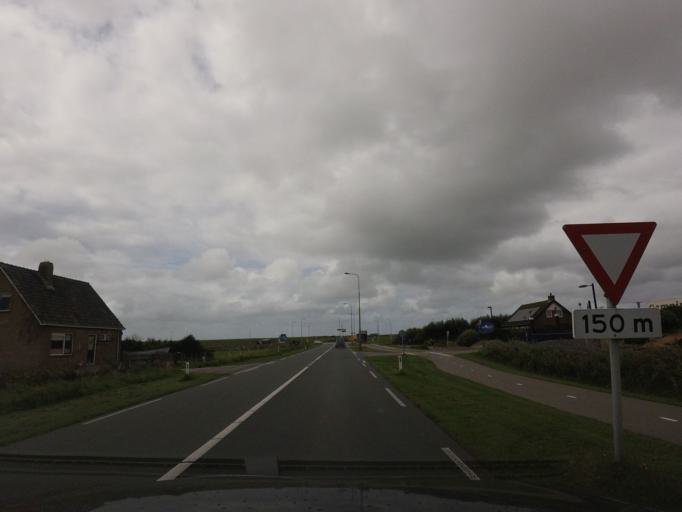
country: NL
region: North Holland
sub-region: Gemeente Schagen
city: Harenkarspel
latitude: 52.7595
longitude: 4.6628
